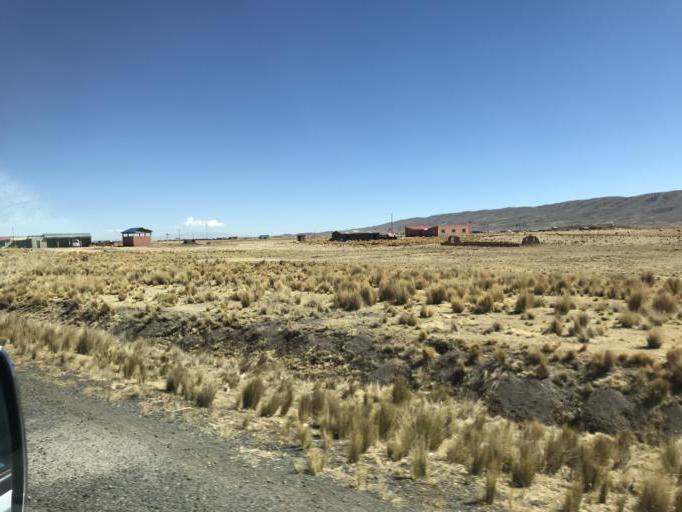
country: BO
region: La Paz
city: Tiahuanaco
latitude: -16.5698
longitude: -68.6658
